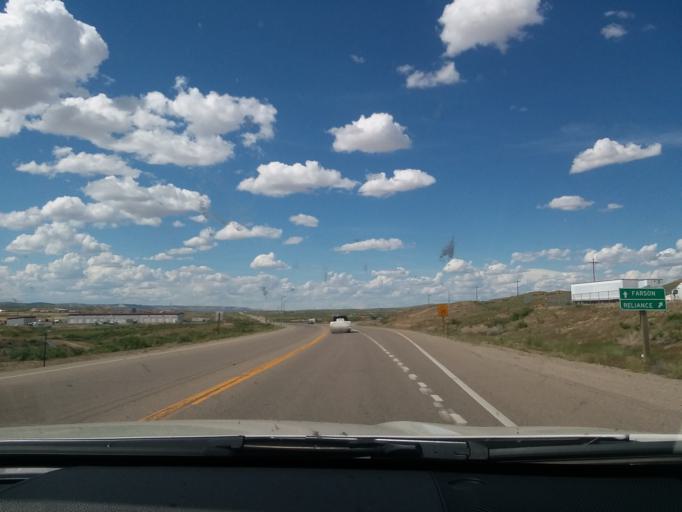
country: US
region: Wyoming
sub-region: Sweetwater County
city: North Rock Springs
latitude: 41.6501
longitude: -109.2275
